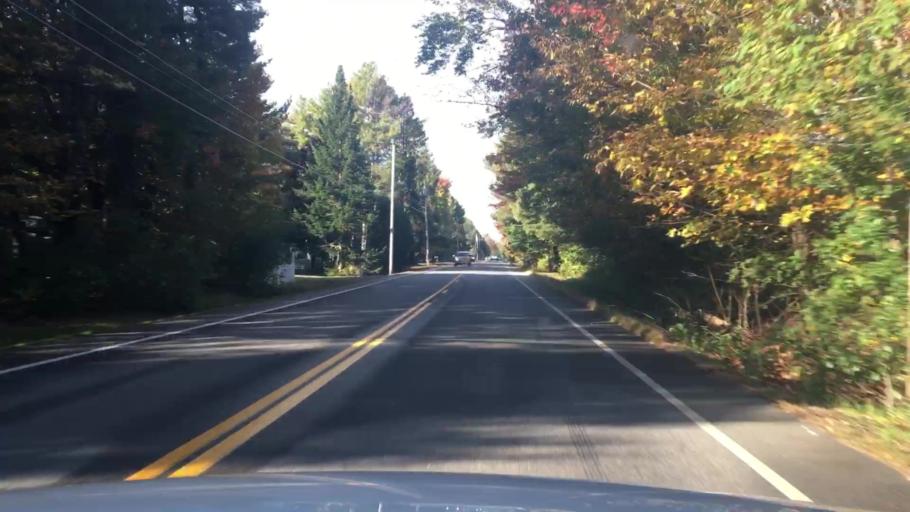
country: US
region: Maine
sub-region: Cumberland County
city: Gorham
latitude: 43.6276
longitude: -70.4568
